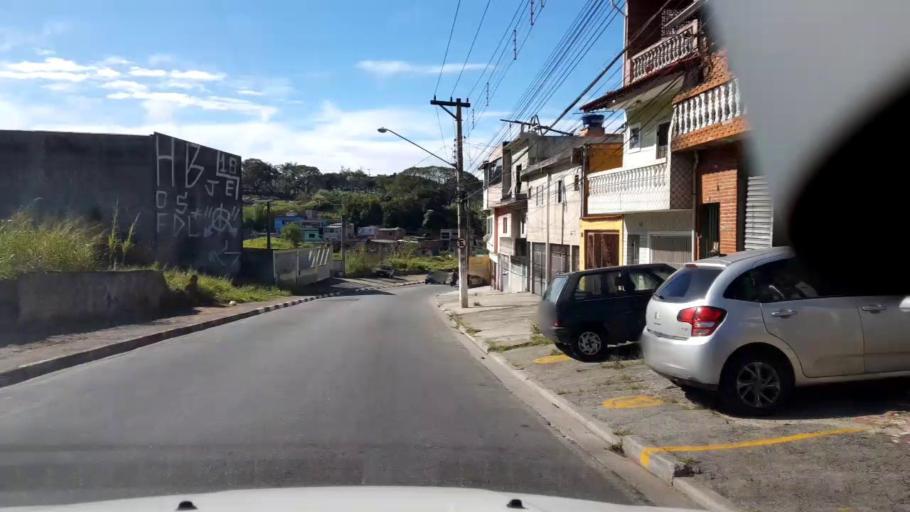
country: BR
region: Sao Paulo
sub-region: Ferraz De Vasconcelos
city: Ferraz de Vasconcelos
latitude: -23.5449
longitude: -46.3814
